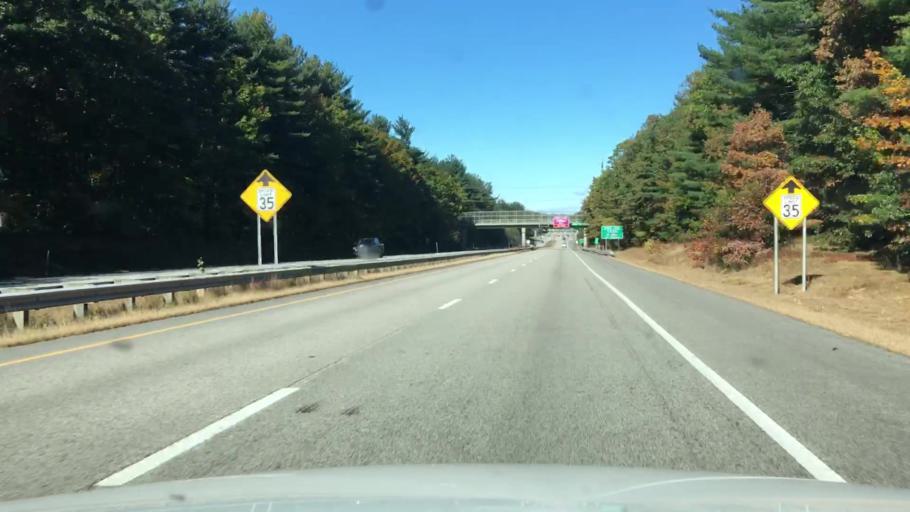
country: US
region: New Hampshire
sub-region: Strafford County
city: Rochester
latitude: 43.2673
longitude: -70.9554
